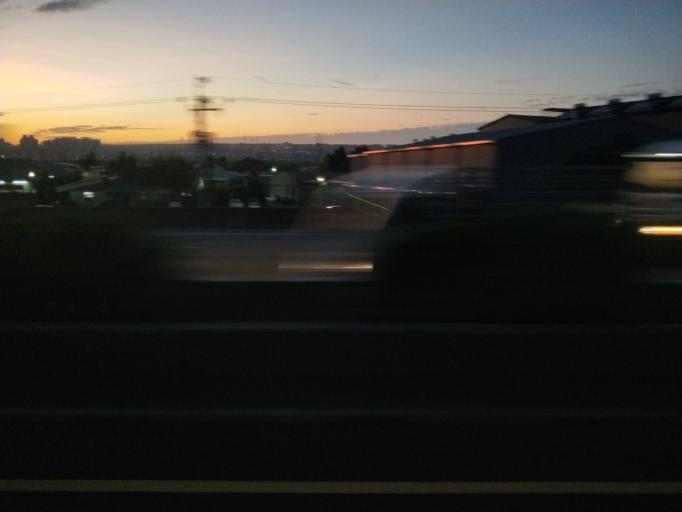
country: TW
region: Taiwan
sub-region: Taichung City
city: Taichung
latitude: 24.1900
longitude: 120.6383
